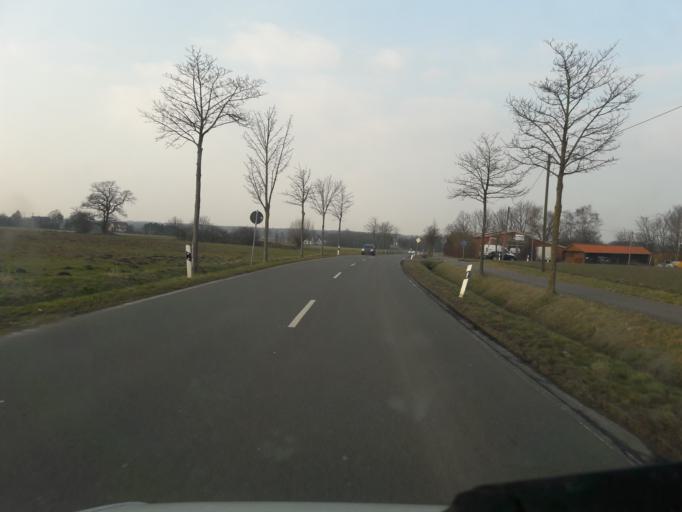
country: DE
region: North Rhine-Westphalia
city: Espelkamp
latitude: 52.3521
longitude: 8.6479
